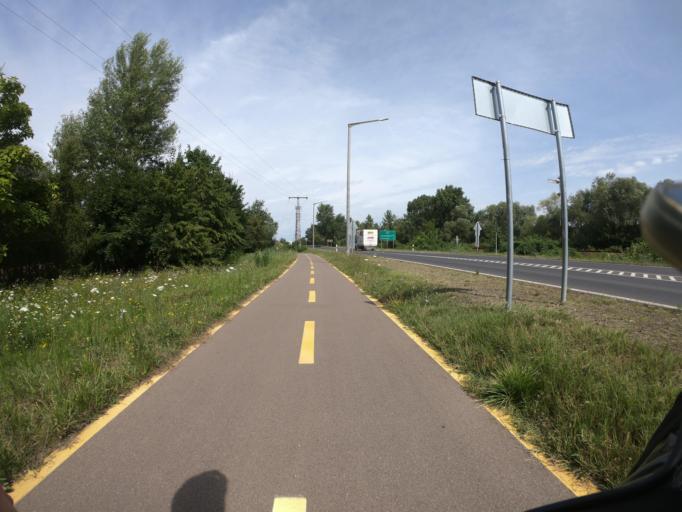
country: HU
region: Jasz-Nagykun-Szolnok
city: Tiszafured
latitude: 47.6288
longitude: 20.7471
